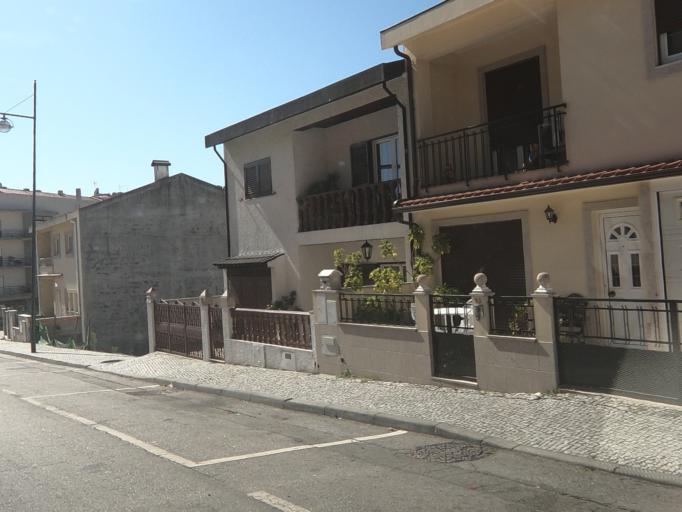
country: PT
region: Vila Real
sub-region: Santa Marta de Penaguiao
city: Santa Marta de Penaguiao
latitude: 41.2122
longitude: -7.7847
